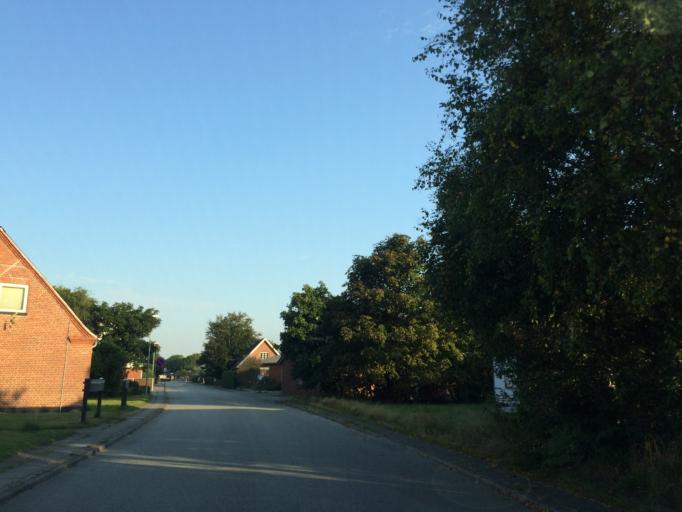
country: DK
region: Central Jutland
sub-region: Holstebro Kommune
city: Ulfborg
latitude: 56.2733
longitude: 8.3246
